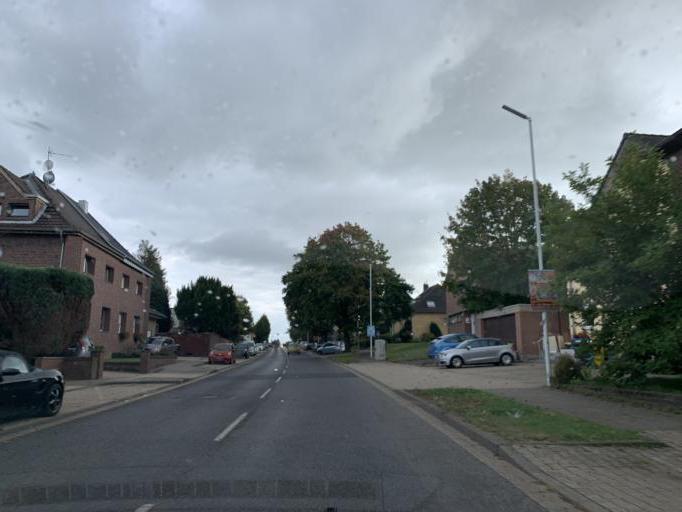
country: DE
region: North Rhine-Westphalia
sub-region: Regierungsbezirk Koln
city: Linnich
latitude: 50.9751
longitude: 6.2690
